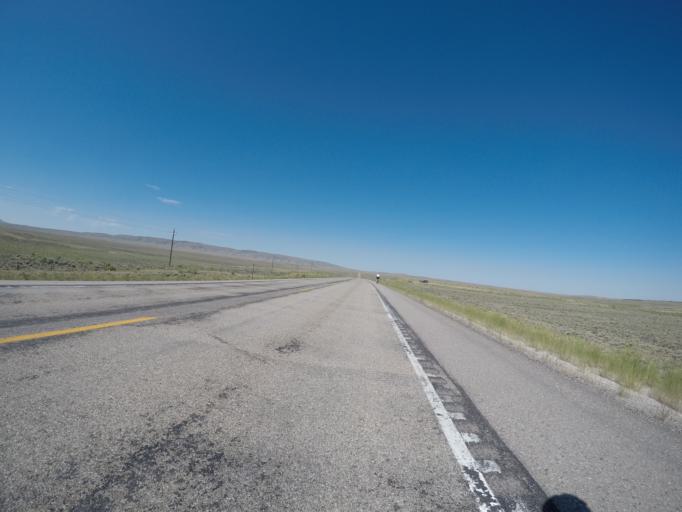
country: US
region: Wyoming
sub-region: Carbon County
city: Saratoga
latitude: 41.8241
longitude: -106.6459
